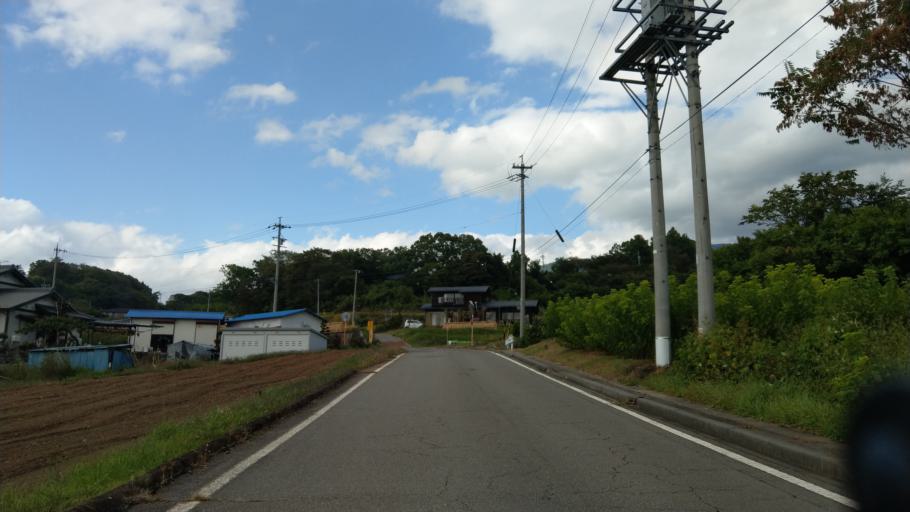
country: JP
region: Nagano
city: Komoro
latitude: 36.3473
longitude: 138.4138
